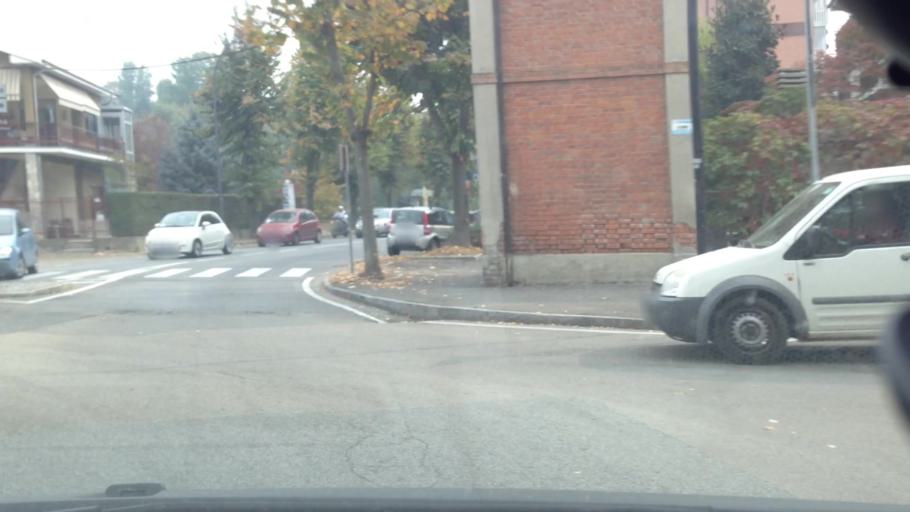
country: IT
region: Piedmont
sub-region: Provincia di Asti
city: Asti
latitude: 44.9072
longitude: 8.1909
